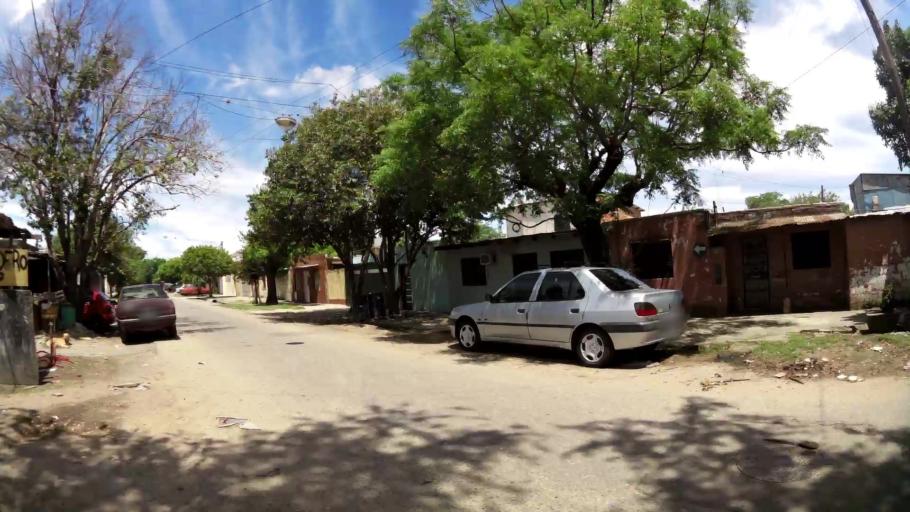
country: AR
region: Santa Fe
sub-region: Departamento de Rosario
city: Rosario
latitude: -32.9807
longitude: -60.6307
